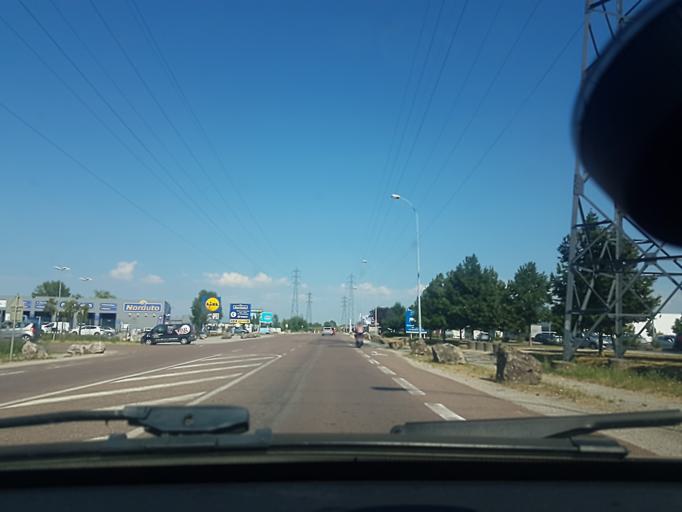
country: FR
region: Bourgogne
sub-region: Departement de Saone-et-Loire
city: Chalon-sur-Saone
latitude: 46.7725
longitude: 4.8669
